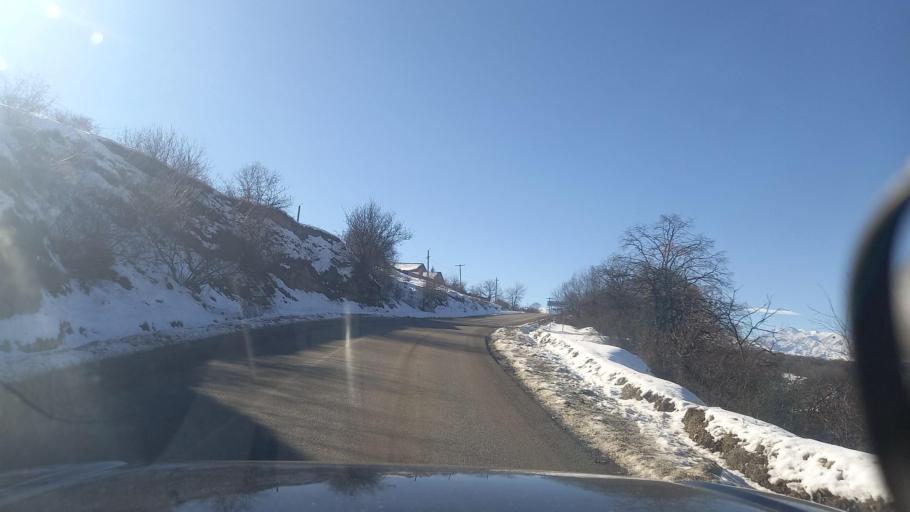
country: RU
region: North Ossetia
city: Chikola
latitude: 43.2284
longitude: 43.9306
